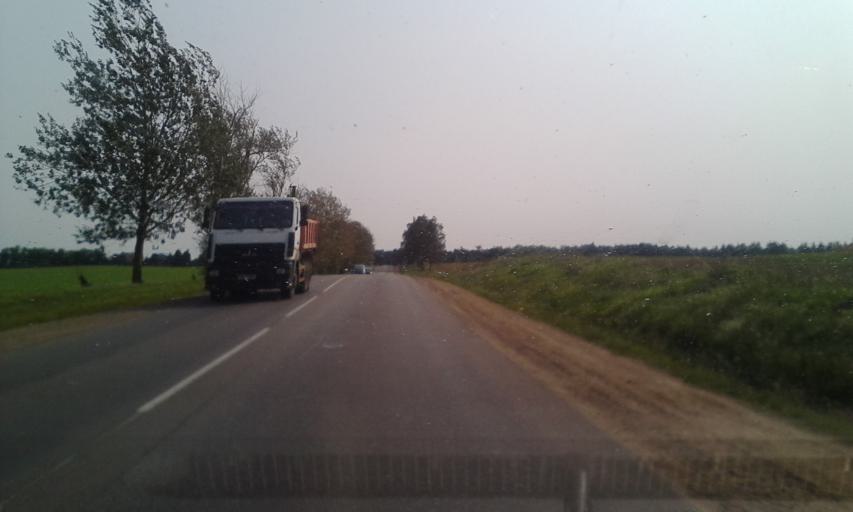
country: BY
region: Minsk
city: Hatava
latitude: 53.8199
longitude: 27.6383
